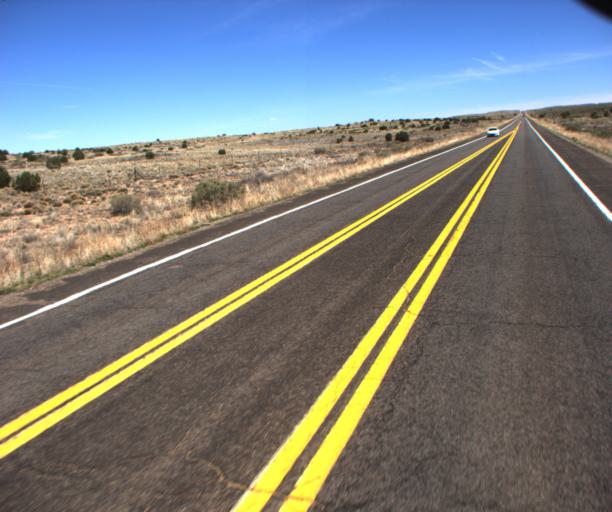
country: US
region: Arizona
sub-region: Mohave County
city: Peach Springs
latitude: 35.5037
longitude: -113.5243
